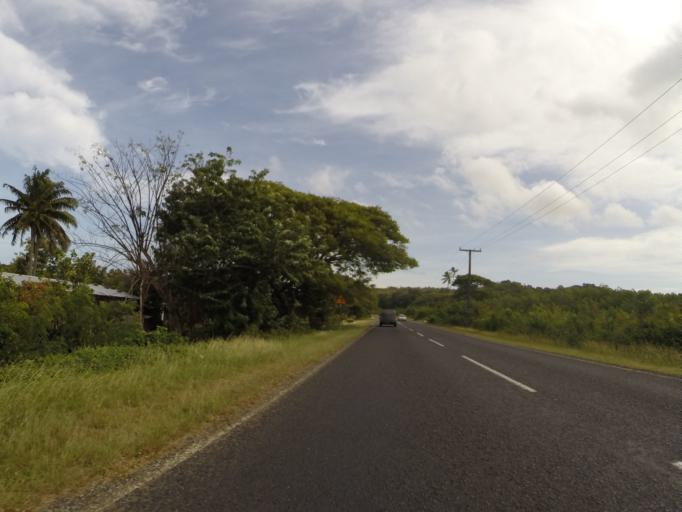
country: FJ
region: Western
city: Nadi
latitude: -18.1525
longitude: 177.4446
